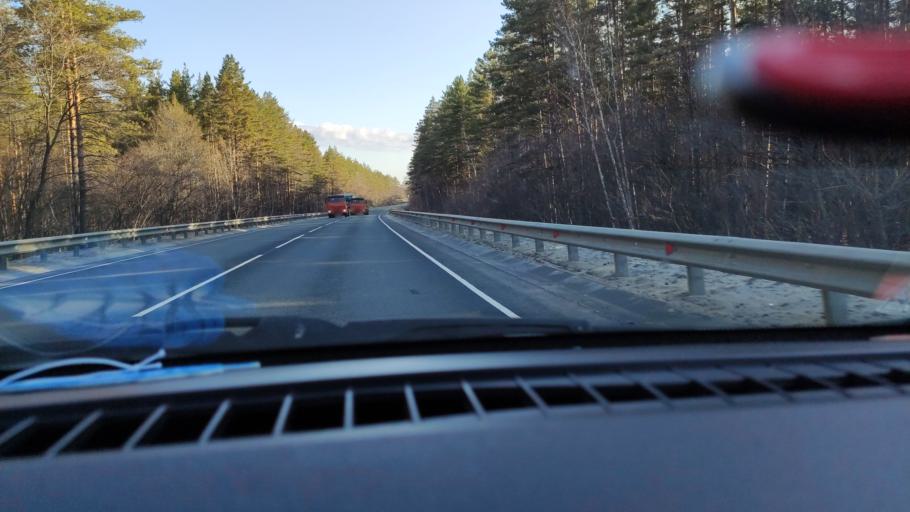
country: RU
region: Saratov
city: Khvalynsk
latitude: 52.5183
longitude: 48.0180
